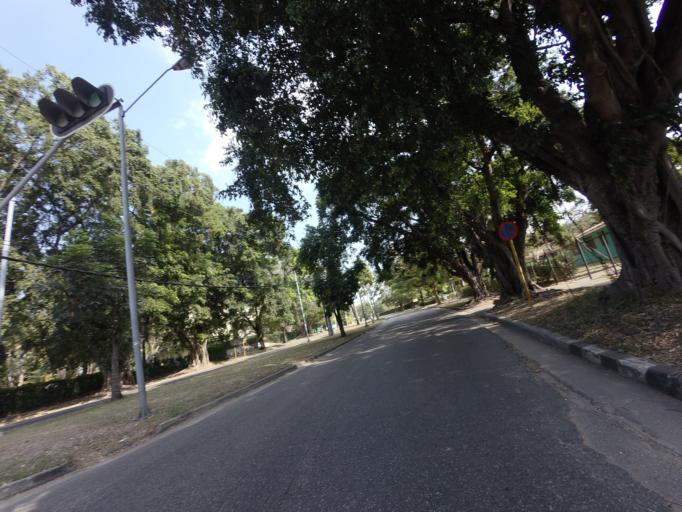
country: CU
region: La Habana
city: Cerro
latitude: 23.0803
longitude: -82.4464
